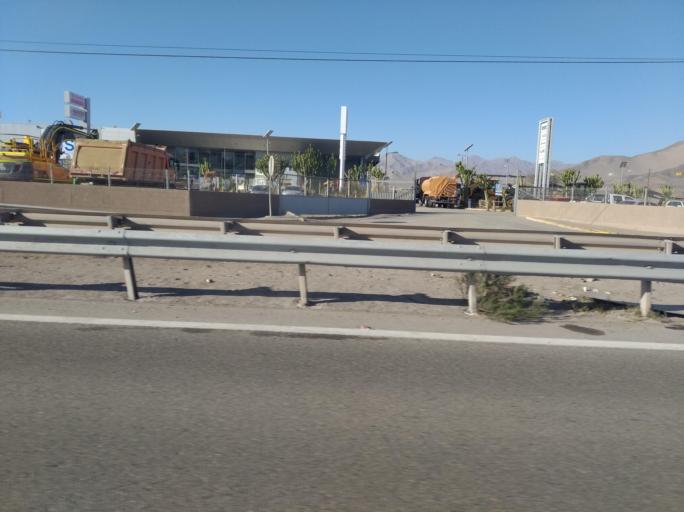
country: CL
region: Atacama
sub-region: Provincia de Copiapo
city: Copiapo
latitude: -27.3304
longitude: -70.3840
